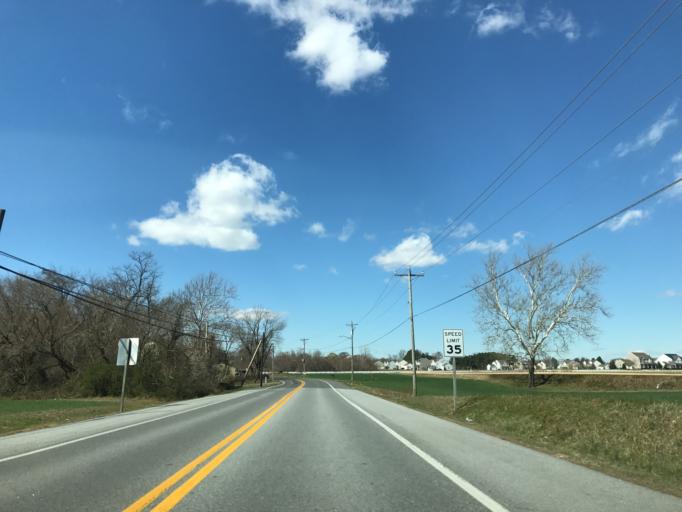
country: US
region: Maryland
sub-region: Queen Anne's County
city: Kingstown
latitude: 39.1378
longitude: -75.9792
